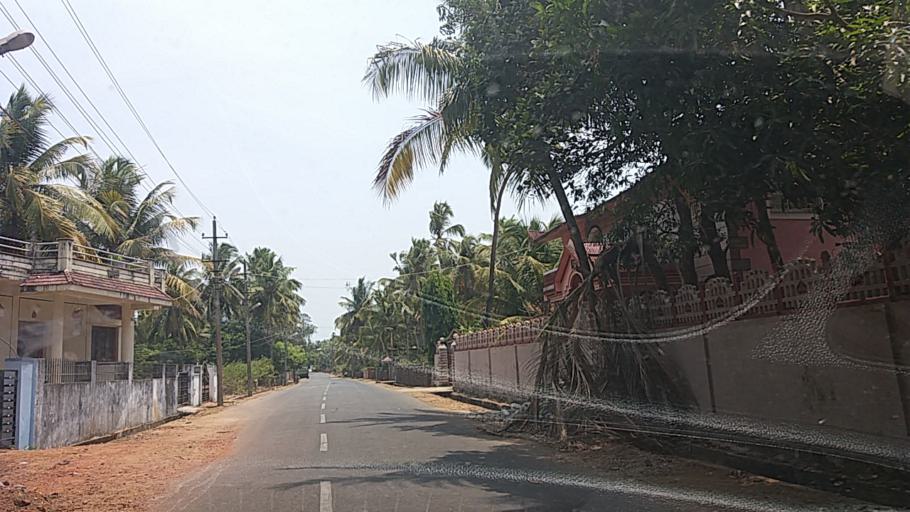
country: IN
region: Karnataka
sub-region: Uttar Kannada
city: Karwar
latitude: 14.8152
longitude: 74.1515
